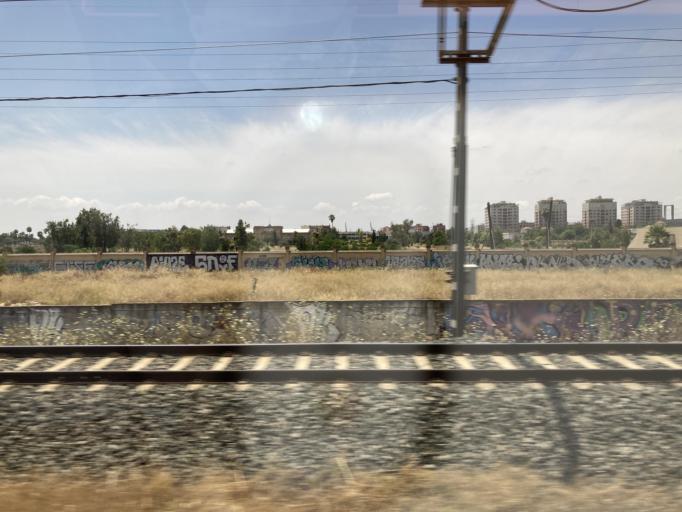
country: ES
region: Andalusia
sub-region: Provincia de Sevilla
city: Sevilla
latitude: 37.3449
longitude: -5.9684
